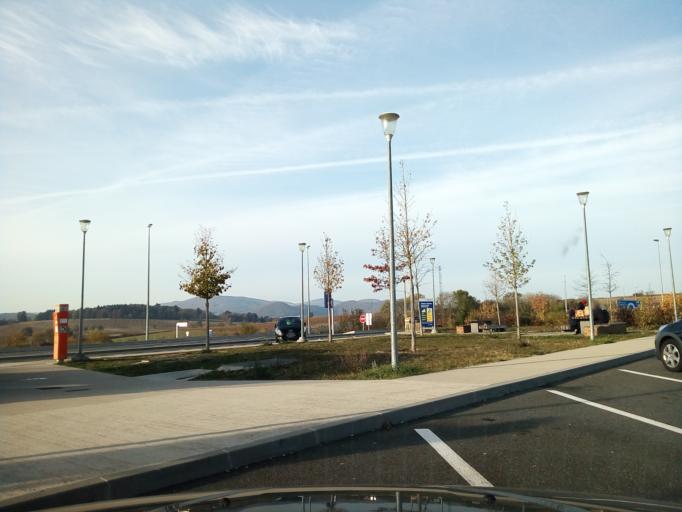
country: FR
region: Rhone-Alpes
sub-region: Departement du Rhone
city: Saint-Germain-Nuelles
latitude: 45.8661
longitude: 4.5968
